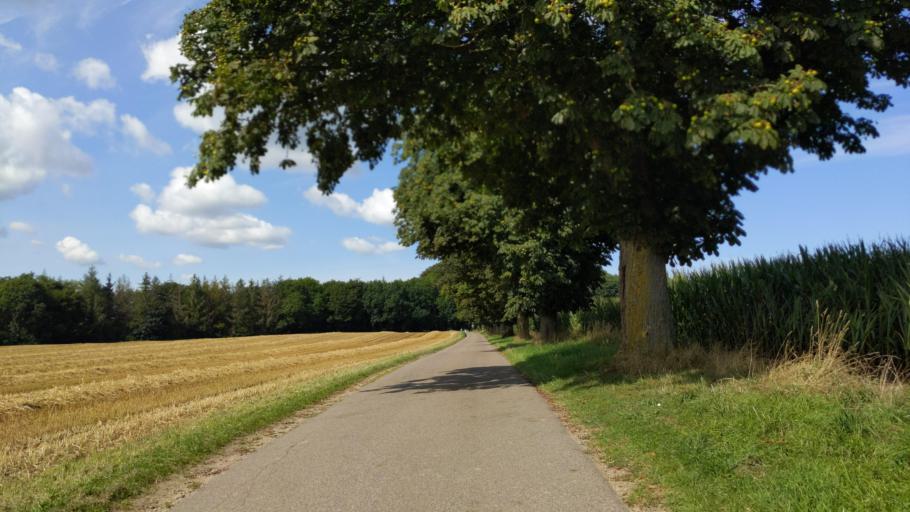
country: DE
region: Schleswig-Holstein
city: Altenkrempe
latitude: 54.1452
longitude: 10.8106
